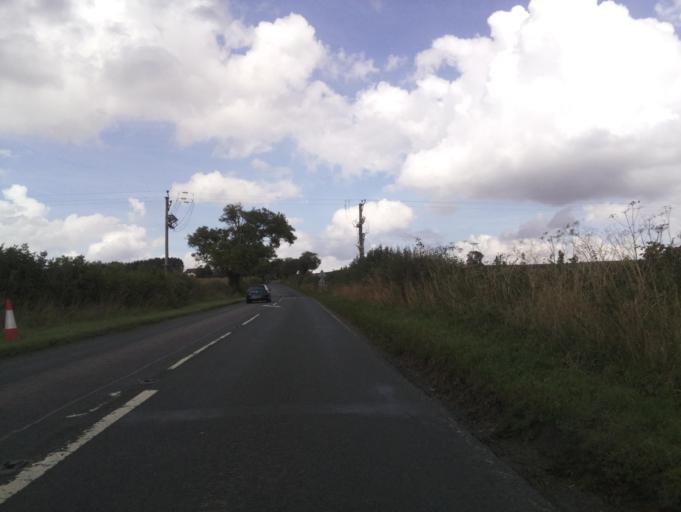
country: GB
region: England
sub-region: North Yorkshire
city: Catterick Garrison
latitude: 54.4305
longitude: -1.6805
